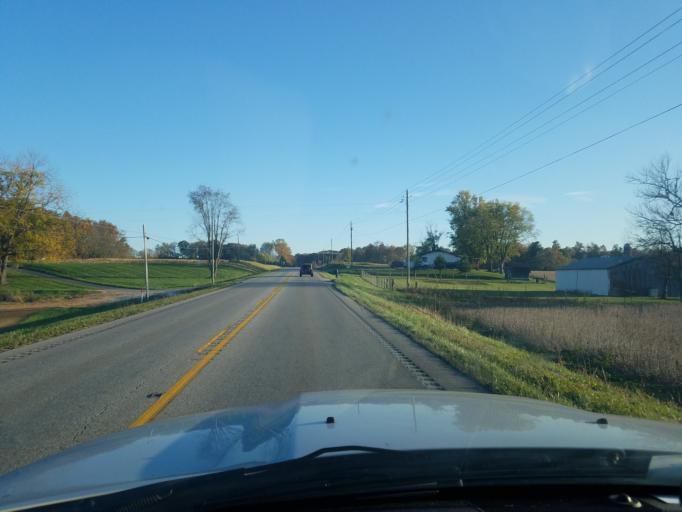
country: US
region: Indiana
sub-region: Washington County
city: New Pekin
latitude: 38.5641
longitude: -86.0464
